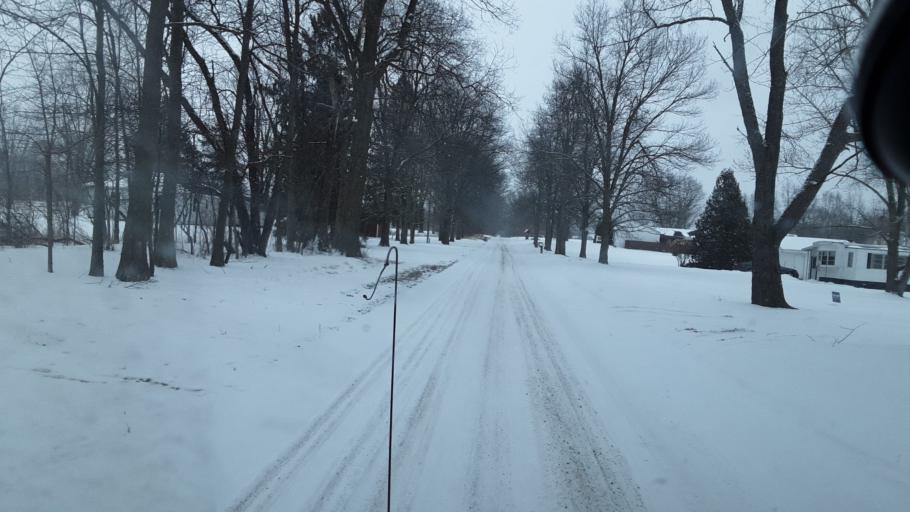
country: US
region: Michigan
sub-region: Ingham County
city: Leslie
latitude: 42.4221
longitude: -84.4703
